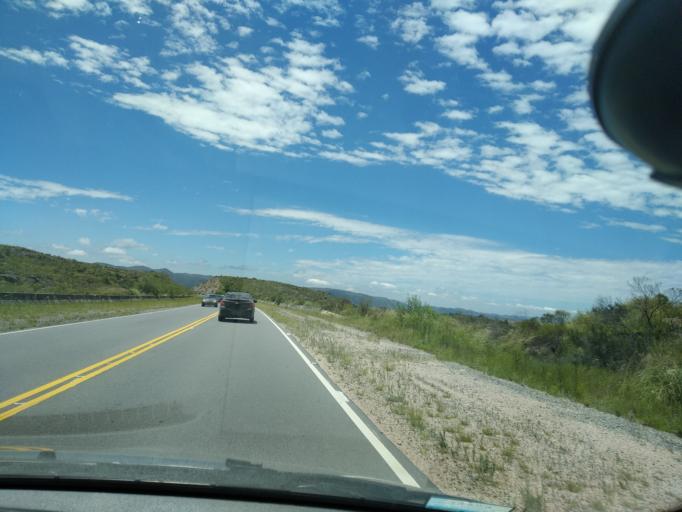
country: AR
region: Cordoba
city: Cuesta Blanca
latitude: -31.5800
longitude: -64.6375
